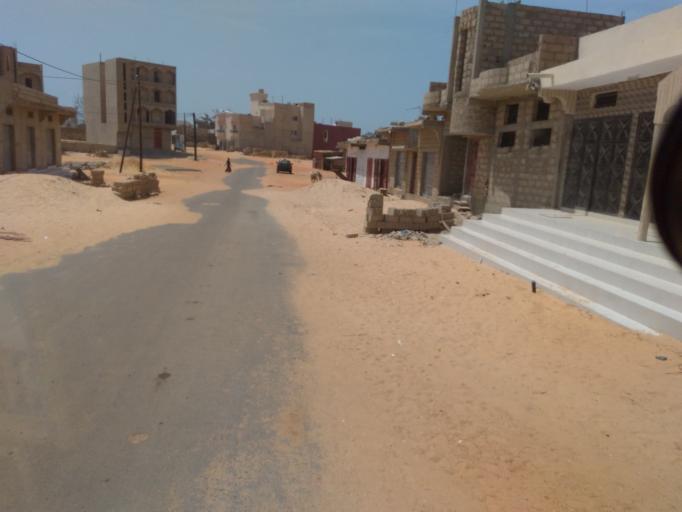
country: SN
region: Dakar
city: Pikine
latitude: 14.7850
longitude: -17.3342
